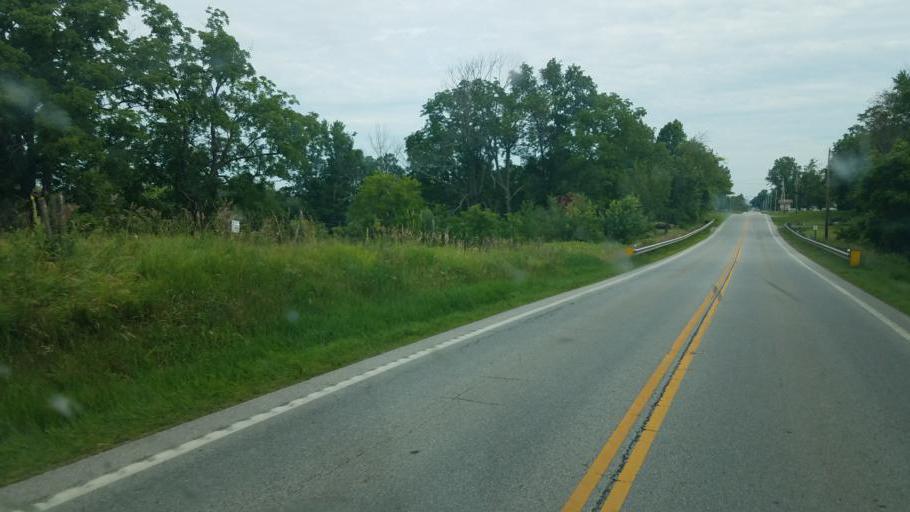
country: US
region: Ohio
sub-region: Lorain County
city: Grafton
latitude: 41.1826
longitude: -82.0227
